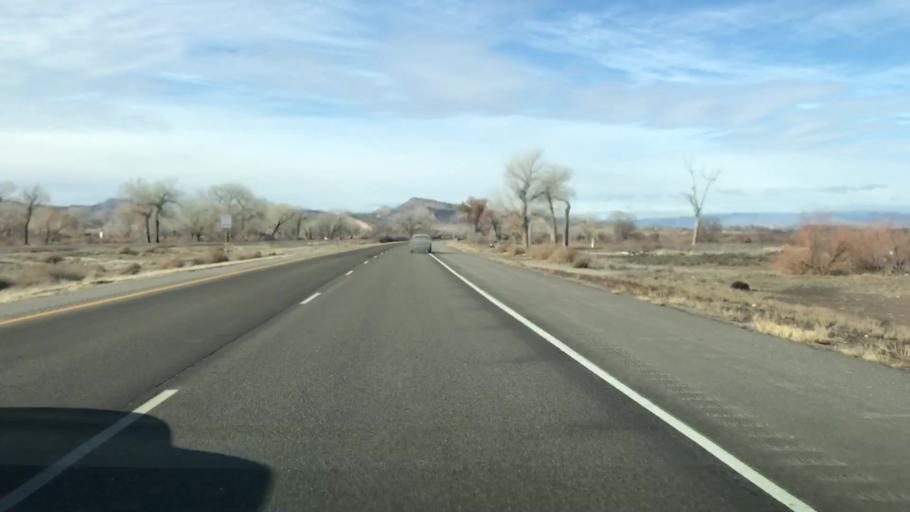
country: US
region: Colorado
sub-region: Mesa County
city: Loma
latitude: 39.1642
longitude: -108.7802
